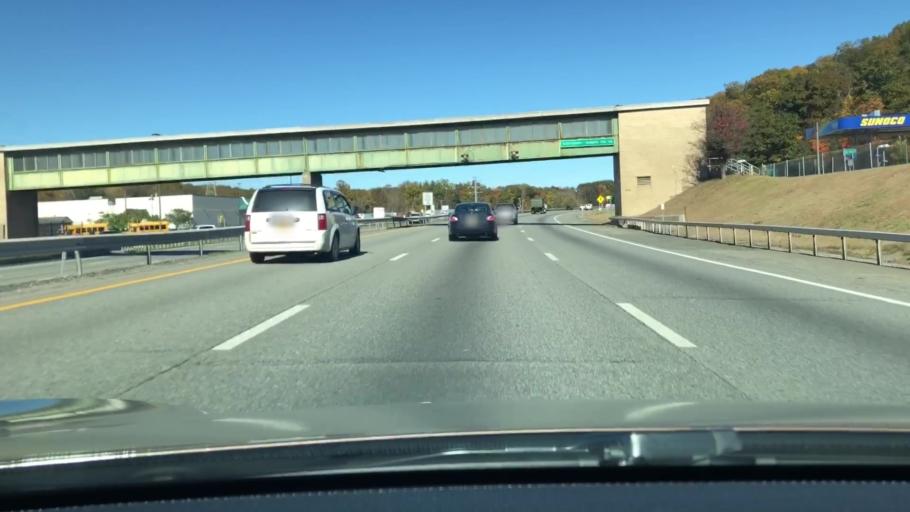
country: US
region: New York
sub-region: Rockland County
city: Sloatsburg
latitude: 41.1518
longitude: -74.1890
